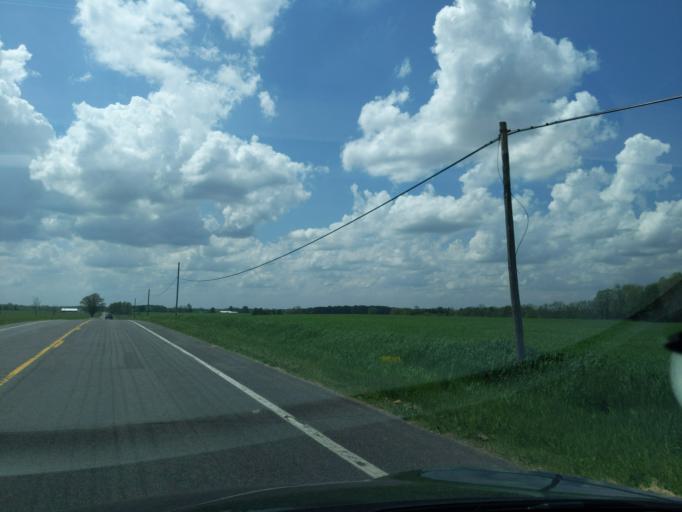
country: US
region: Michigan
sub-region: Ingham County
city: Mason
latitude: 42.5965
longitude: -84.4237
